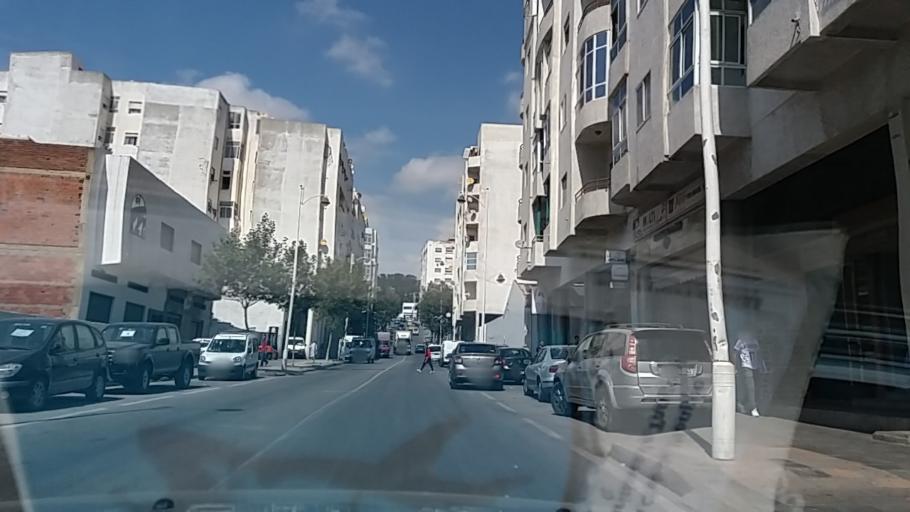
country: MA
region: Tanger-Tetouan
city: Tetouan
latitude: 35.5631
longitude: -5.3687
